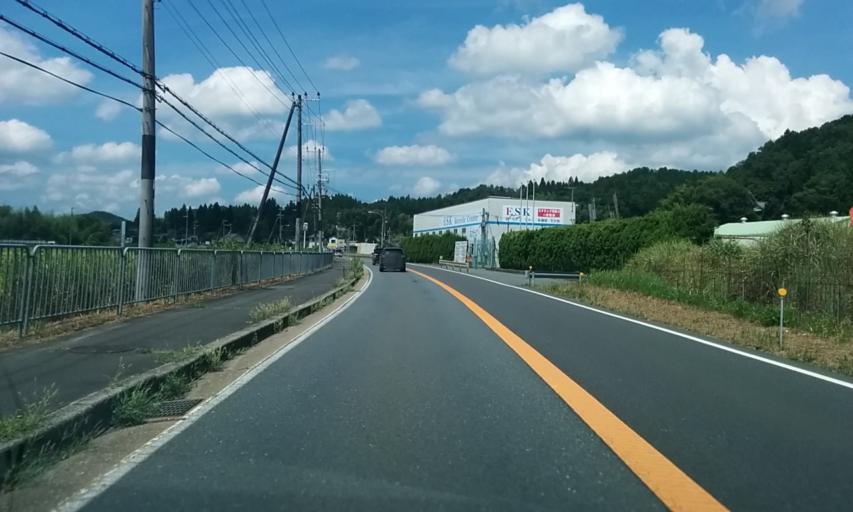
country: JP
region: Kyoto
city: Ayabe
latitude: 35.1801
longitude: 135.3887
